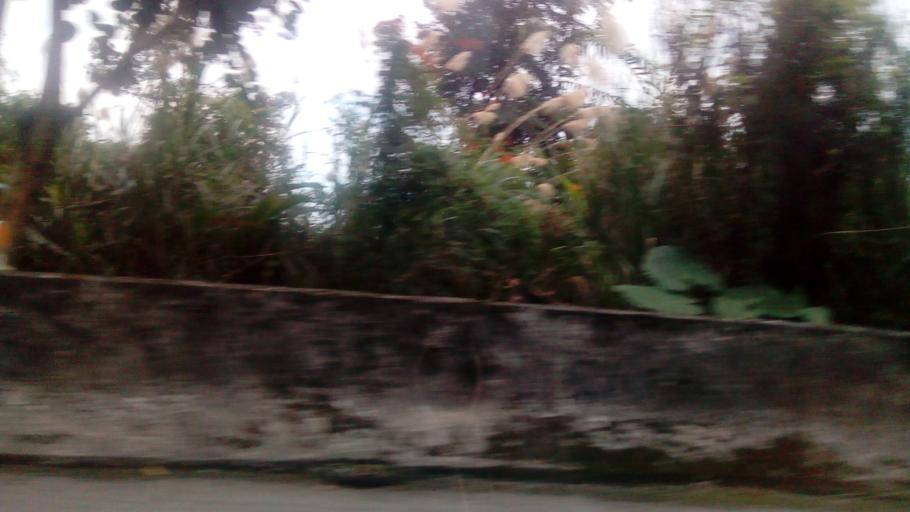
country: TW
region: Taiwan
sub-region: Yilan
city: Yilan
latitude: 24.6352
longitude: 121.5539
